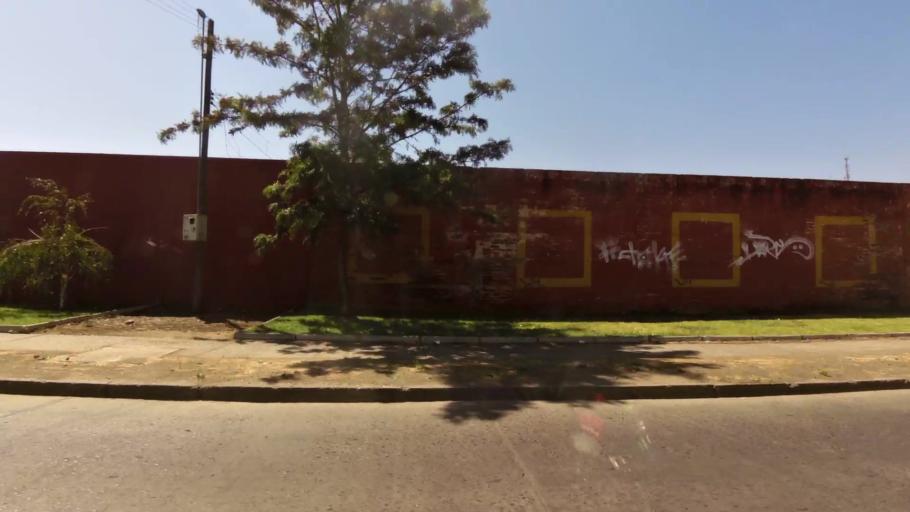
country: CL
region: Maule
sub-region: Provincia de Curico
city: Curico
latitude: -34.9748
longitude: -71.2352
